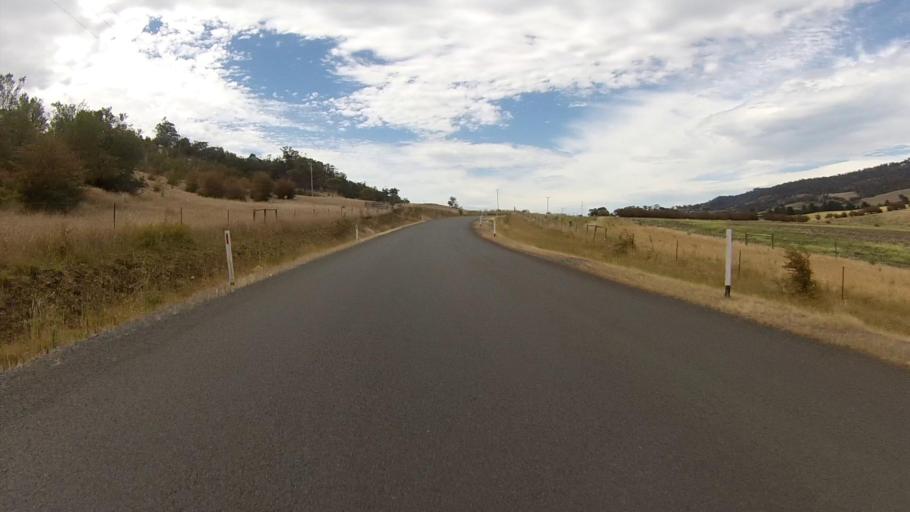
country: AU
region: Tasmania
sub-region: Brighton
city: Old Beach
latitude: -42.7222
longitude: 147.3394
